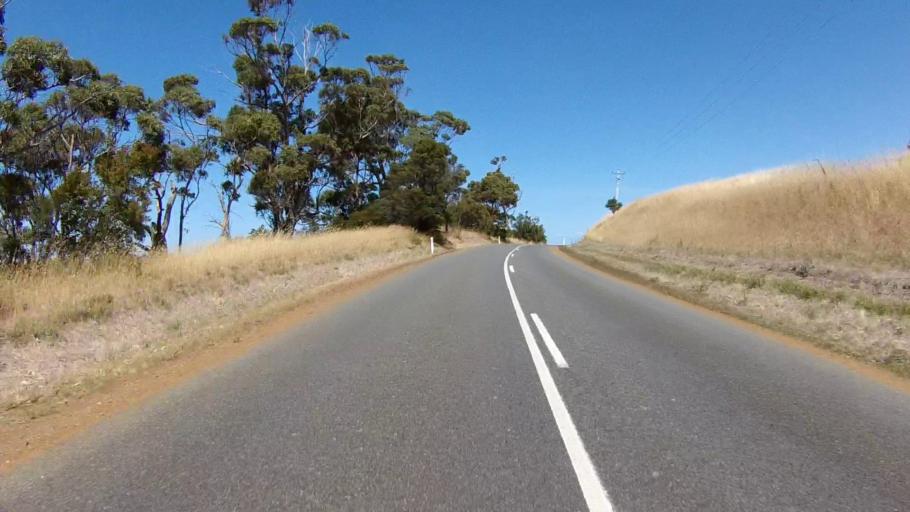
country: AU
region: Tasmania
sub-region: Sorell
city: Sorell
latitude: -42.2666
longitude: 148.0032
